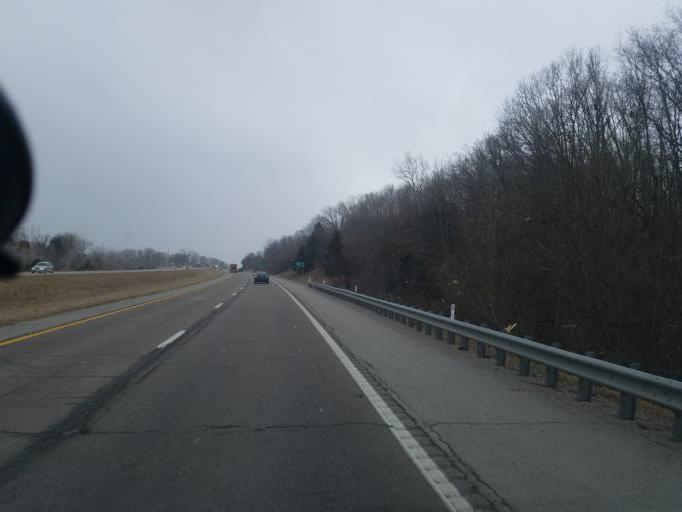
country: US
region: Missouri
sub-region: Boone County
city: Hallsville
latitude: 39.1231
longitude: -92.3324
